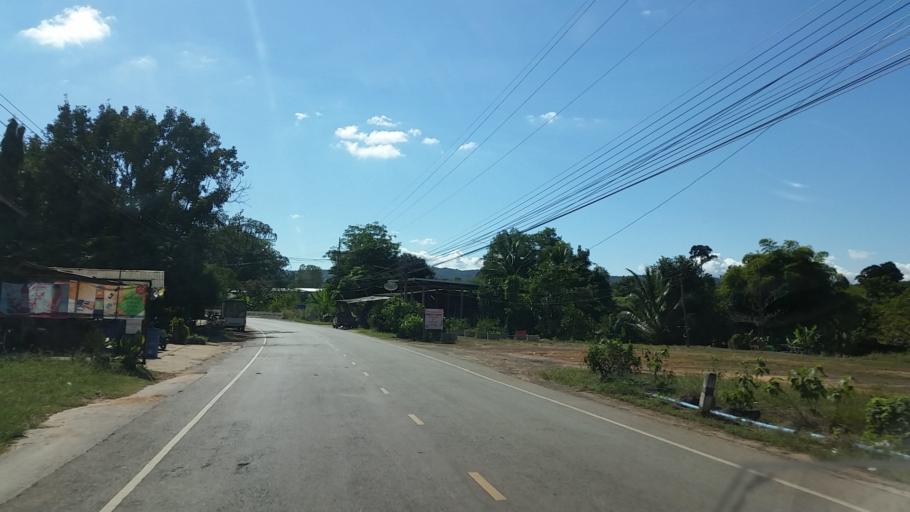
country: TH
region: Chaiyaphum
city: Thep Sathit
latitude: 15.5643
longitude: 101.4132
